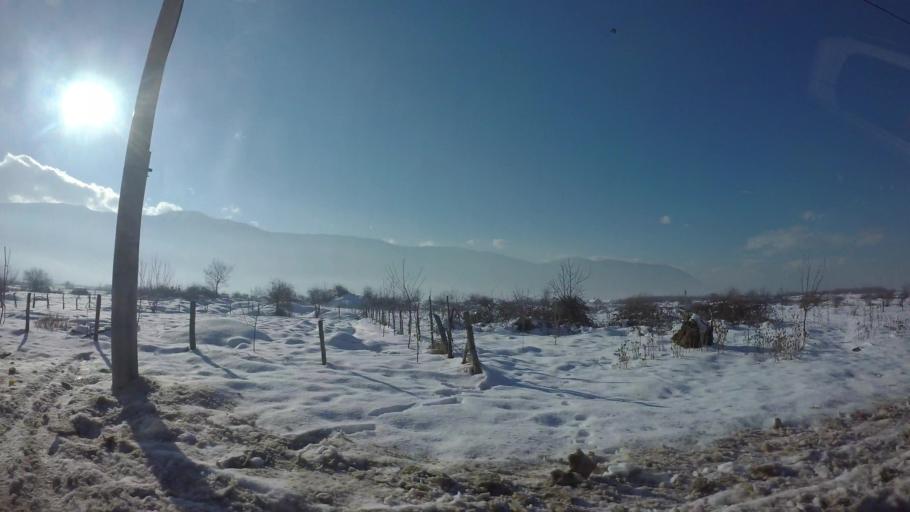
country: BA
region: Federation of Bosnia and Herzegovina
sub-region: Kanton Sarajevo
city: Sarajevo
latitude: 43.8104
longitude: 18.3277
